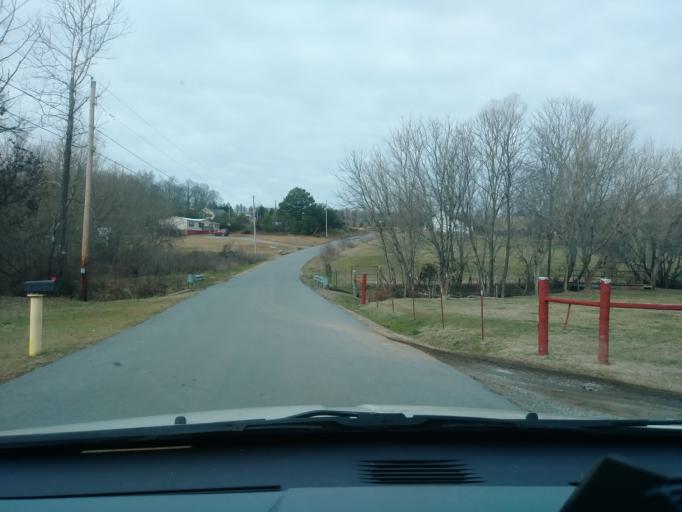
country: US
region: Tennessee
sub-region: Greene County
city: Mosheim
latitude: 36.1052
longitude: -82.9097
